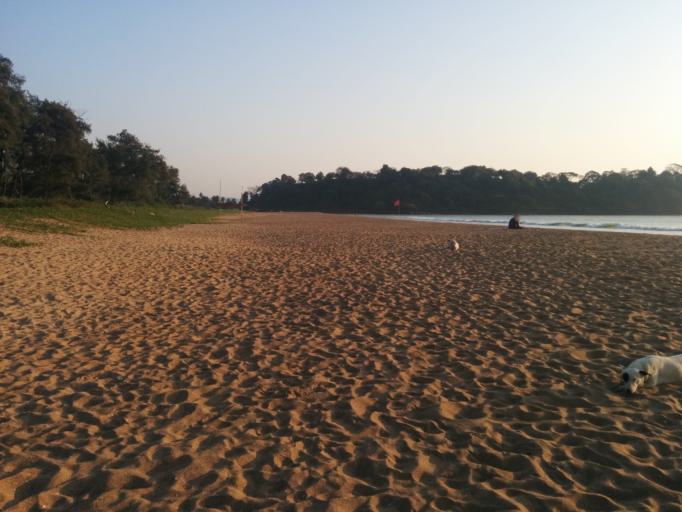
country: IN
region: Karnataka
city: Canacona
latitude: 14.9888
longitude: 74.0376
